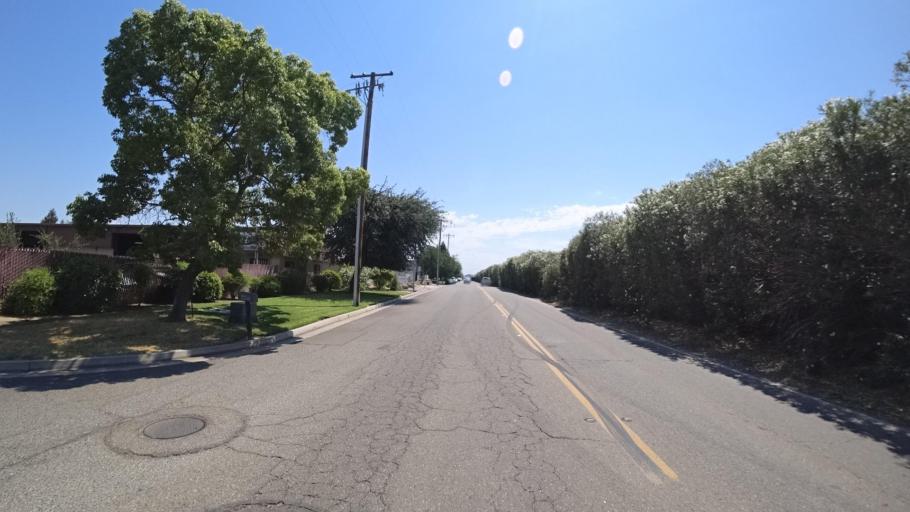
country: US
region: California
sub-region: Fresno County
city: Tarpey Village
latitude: 36.7722
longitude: -119.6898
